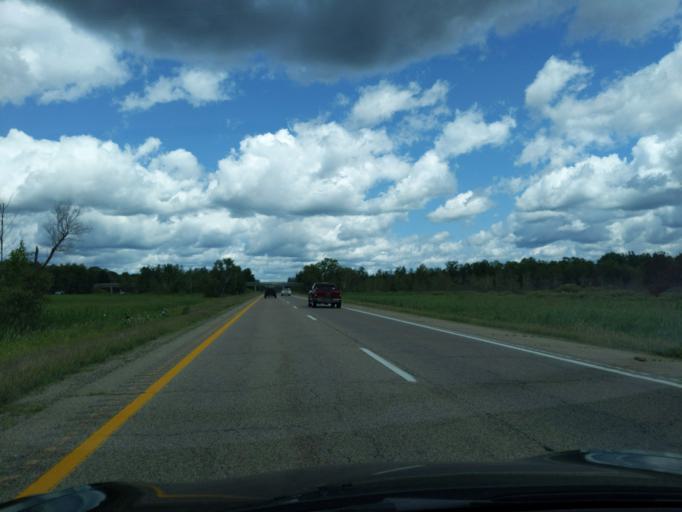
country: US
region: Michigan
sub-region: Roscommon County
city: Houghton Lake
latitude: 44.3996
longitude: -84.7999
